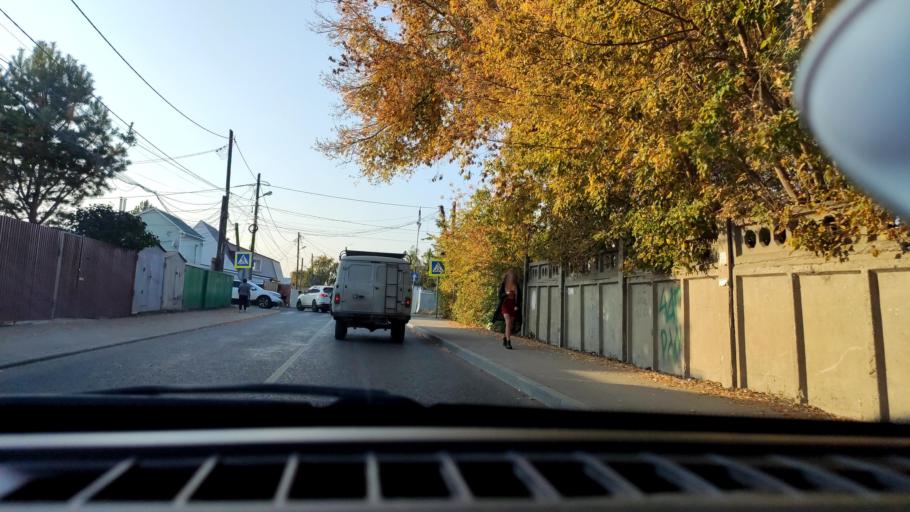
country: RU
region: Samara
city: Samara
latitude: 53.2236
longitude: 50.1871
